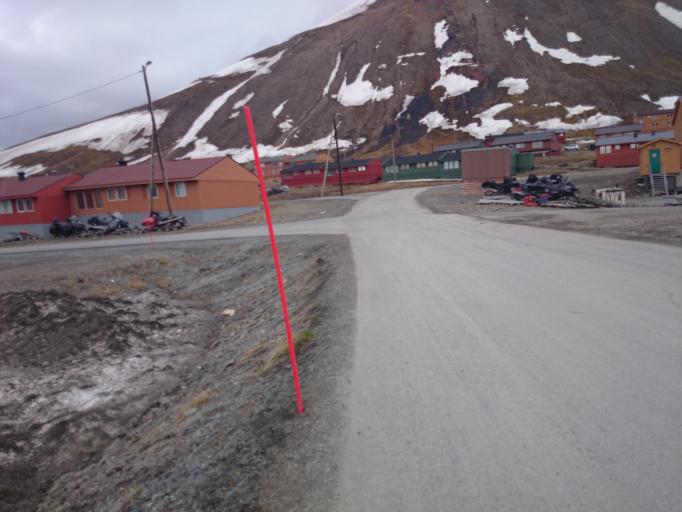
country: SJ
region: Svalbard
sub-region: Spitsbergen
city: Longyearbyen
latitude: 78.2173
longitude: 15.6318
